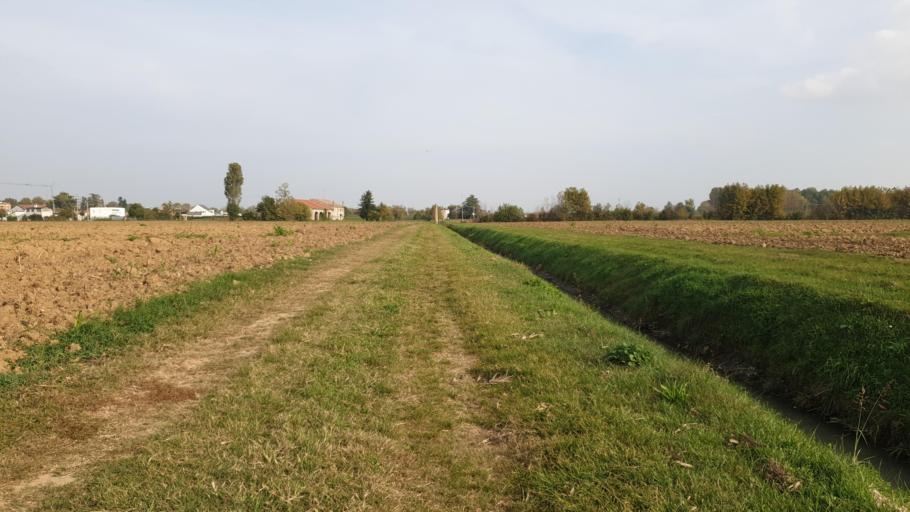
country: IT
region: Veneto
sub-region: Provincia di Padova
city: Ponte San Nicolo
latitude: 45.3397
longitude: 11.9304
